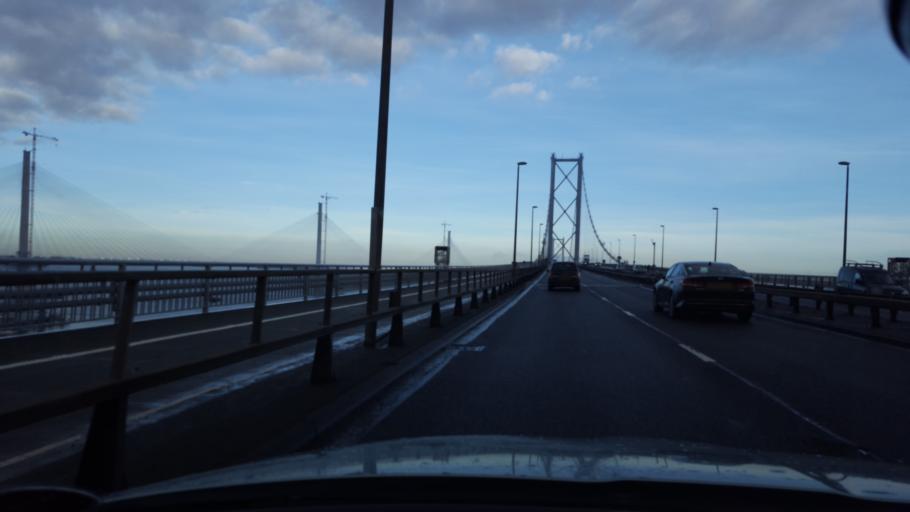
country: GB
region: Scotland
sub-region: Edinburgh
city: Queensferry
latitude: 55.9916
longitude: -3.4049
